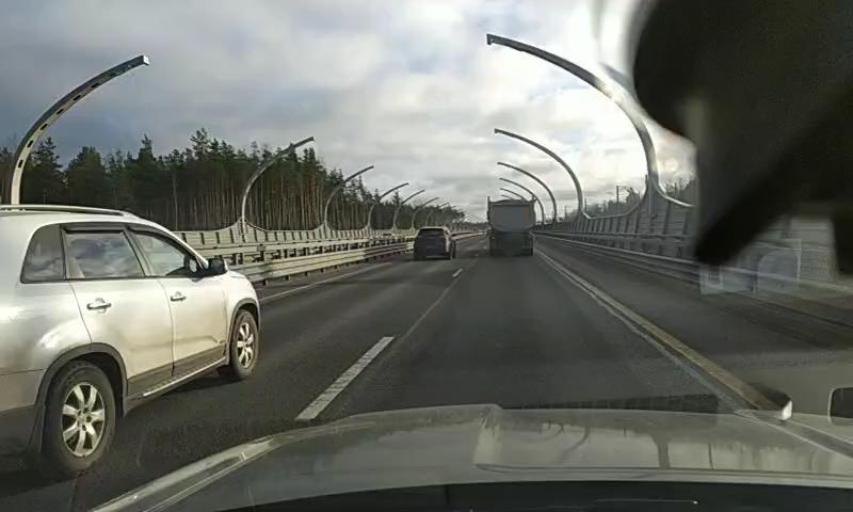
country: RU
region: St.-Petersburg
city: Beloostrov
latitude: 60.1406
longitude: 30.0331
